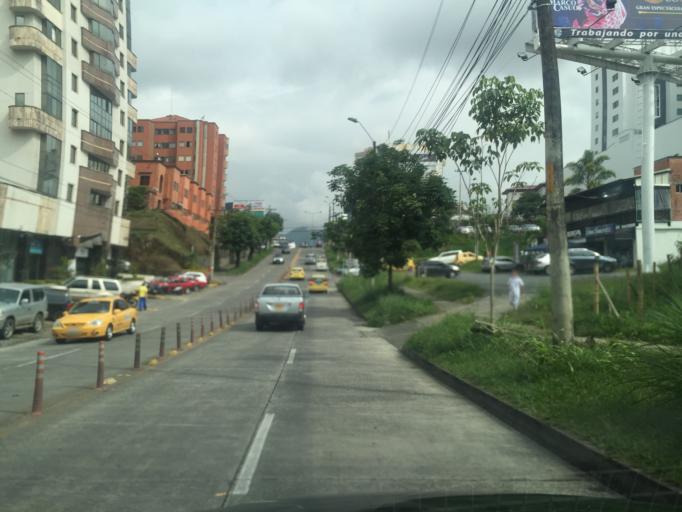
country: CO
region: Risaralda
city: Pereira
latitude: 4.8031
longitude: -75.6913
